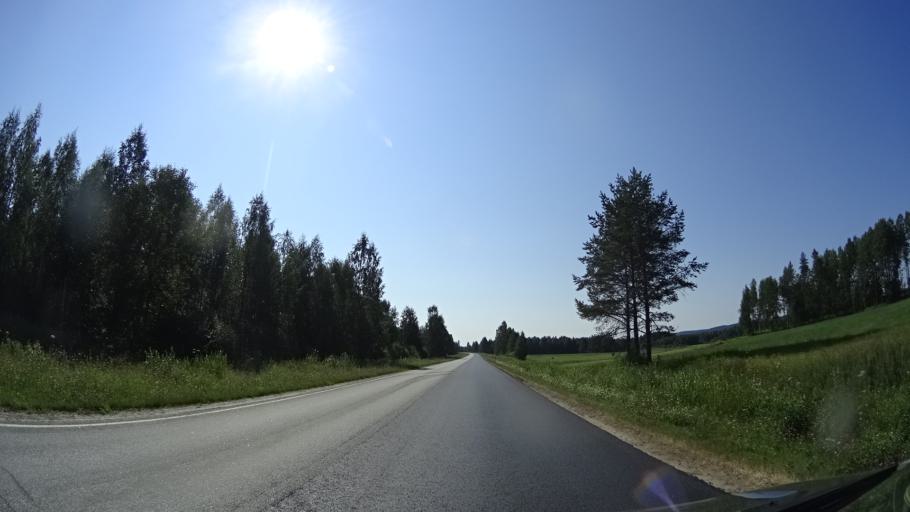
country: FI
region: North Karelia
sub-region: Joensuu
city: Juuka
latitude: 63.2169
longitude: 29.3026
